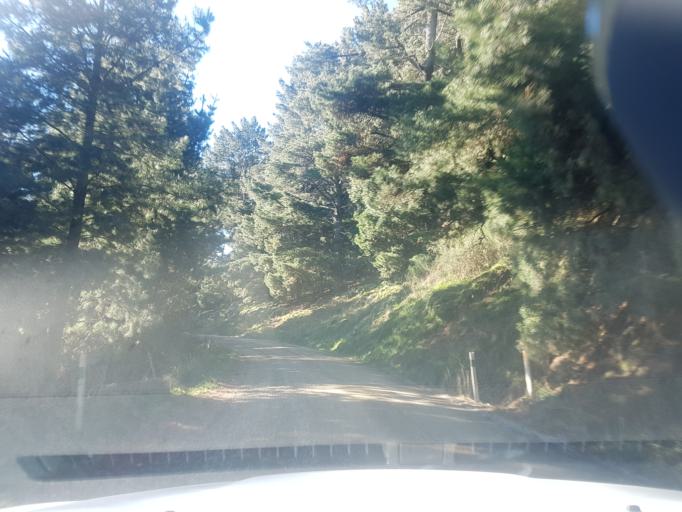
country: NZ
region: Canterbury
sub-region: Timaru District
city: Pleasant Point
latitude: -44.3451
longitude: 171.0760
